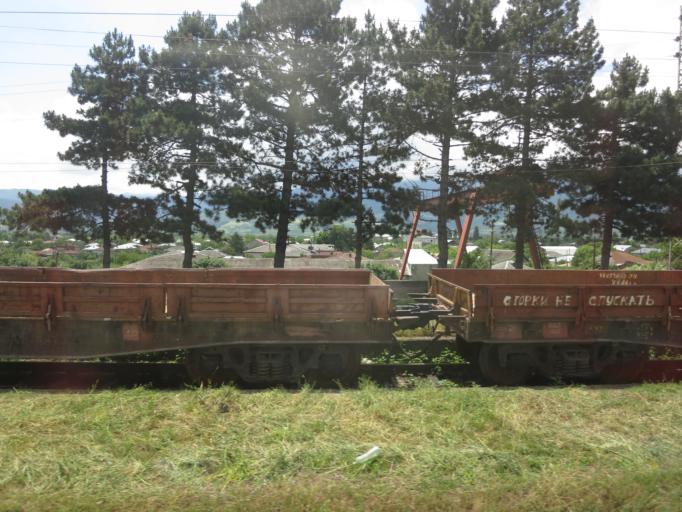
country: GE
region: Shida Kartli
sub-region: Khashuris Raioni
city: Khashuri
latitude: 41.9999
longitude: 43.6073
